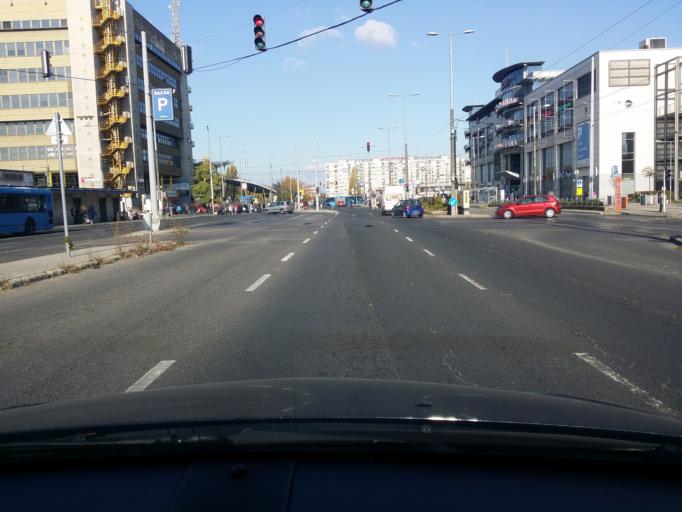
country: HU
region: Budapest
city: Budapest X. keruelet
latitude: 47.5015
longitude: 19.1369
